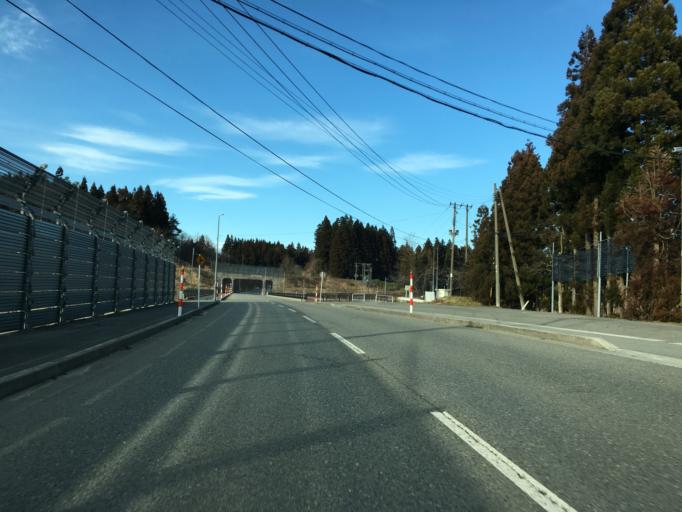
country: JP
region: Yamagata
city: Nagai
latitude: 38.0183
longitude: 139.9713
